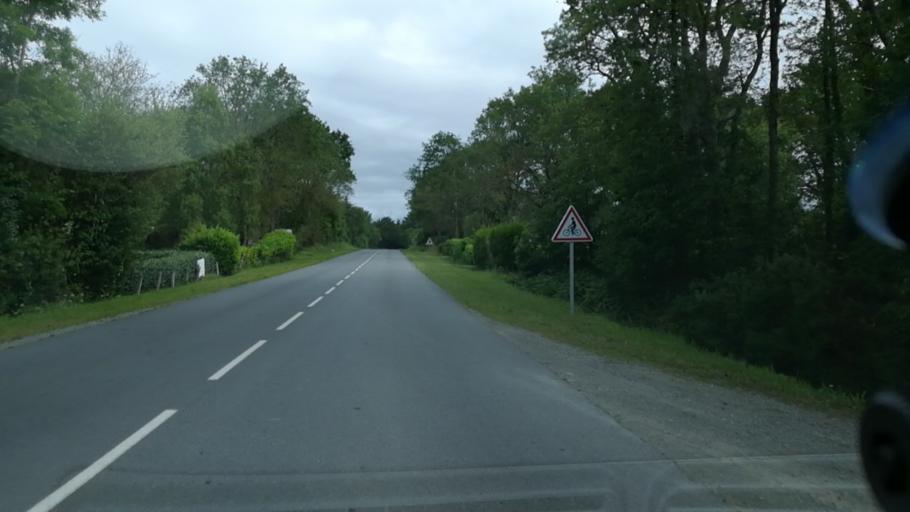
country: FR
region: Brittany
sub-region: Departement du Morbihan
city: Penestin
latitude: 47.4653
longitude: -2.4785
